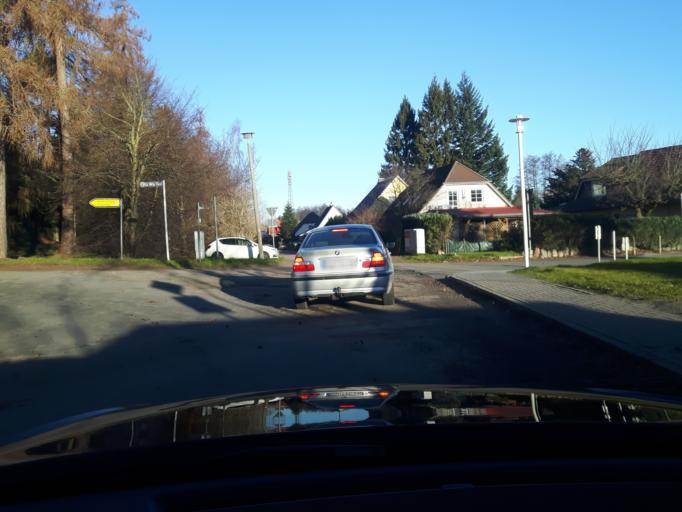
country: DE
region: Mecklenburg-Vorpommern
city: Putbus
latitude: 54.3528
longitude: 13.4640
